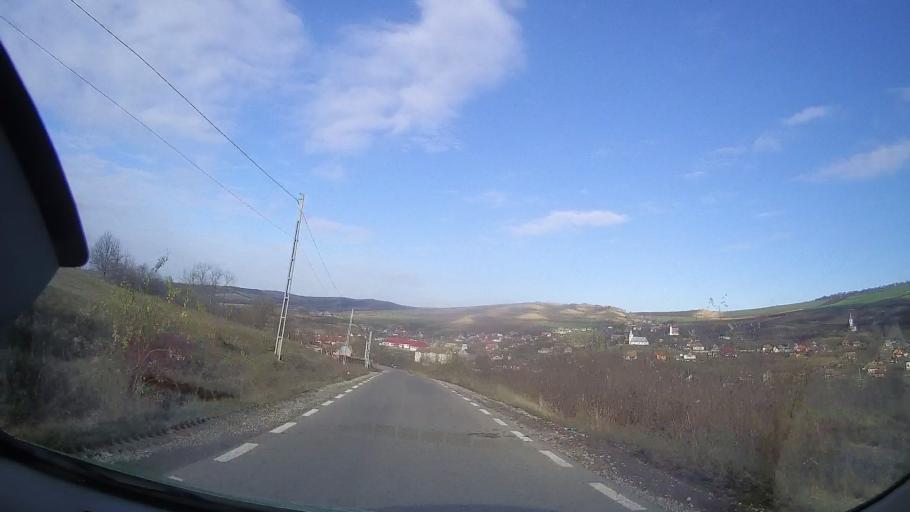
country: RO
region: Mures
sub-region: Comuna Sanger
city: Sanger
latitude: 46.5538
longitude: 24.1425
